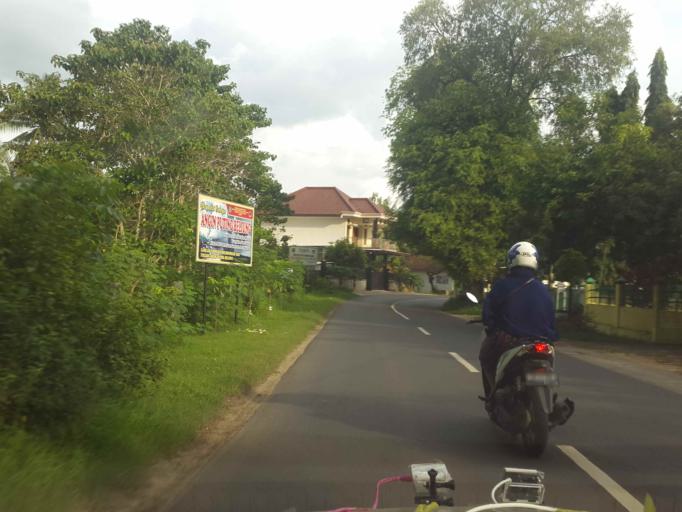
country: ID
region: East Java
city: Senmasen
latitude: -6.9862
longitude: 113.8629
